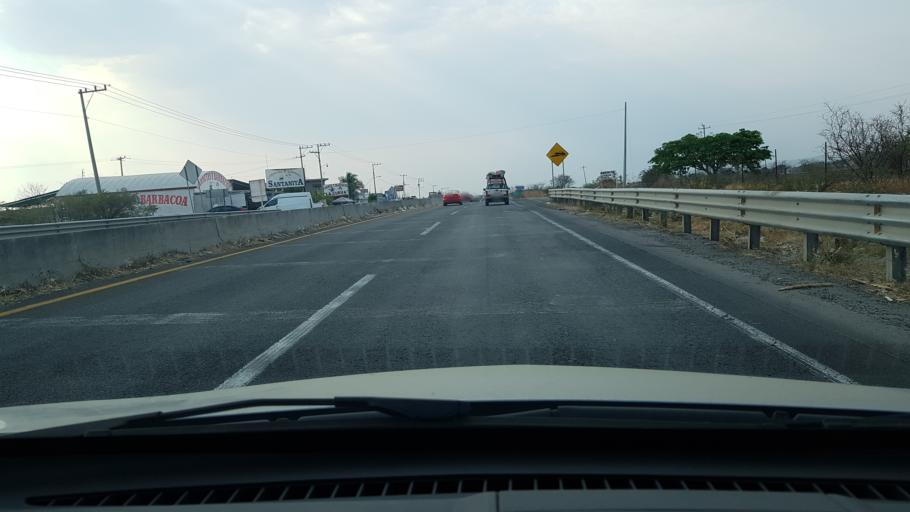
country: MX
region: Morelos
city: Amayuca
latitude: 18.7222
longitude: -98.8044
